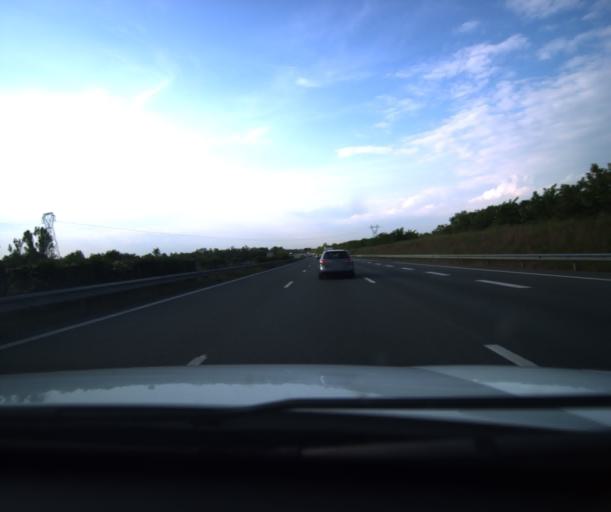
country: FR
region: Midi-Pyrenees
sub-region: Departement du Tarn-et-Garonne
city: Campsas
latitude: 43.8917
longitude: 1.3174
